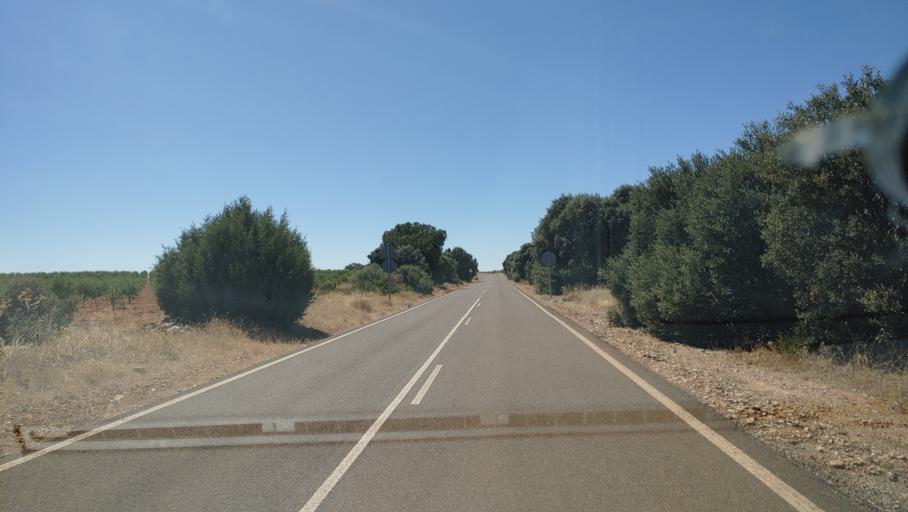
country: ES
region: Castille-La Mancha
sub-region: Provincia de Ciudad Real
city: Villahermosa
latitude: 38.8345
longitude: -2.8214
